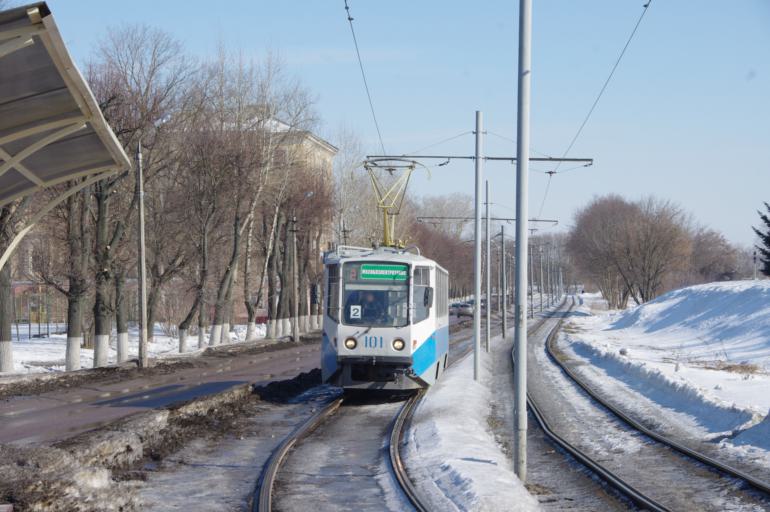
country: RU
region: Moskovskaya
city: Kolomna
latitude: 55.0750
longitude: 38.8020
